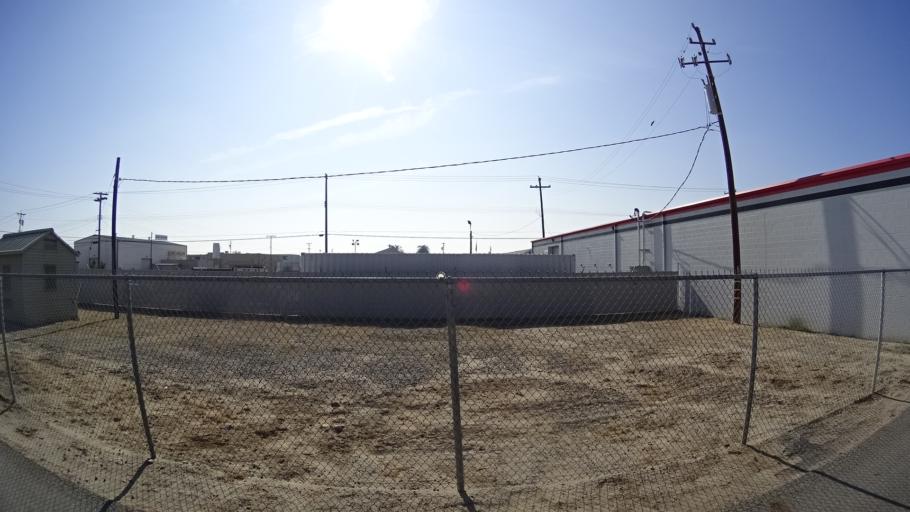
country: US
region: California
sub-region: Kern County
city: Bakersfield
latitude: 35.3818
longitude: -119.0000
